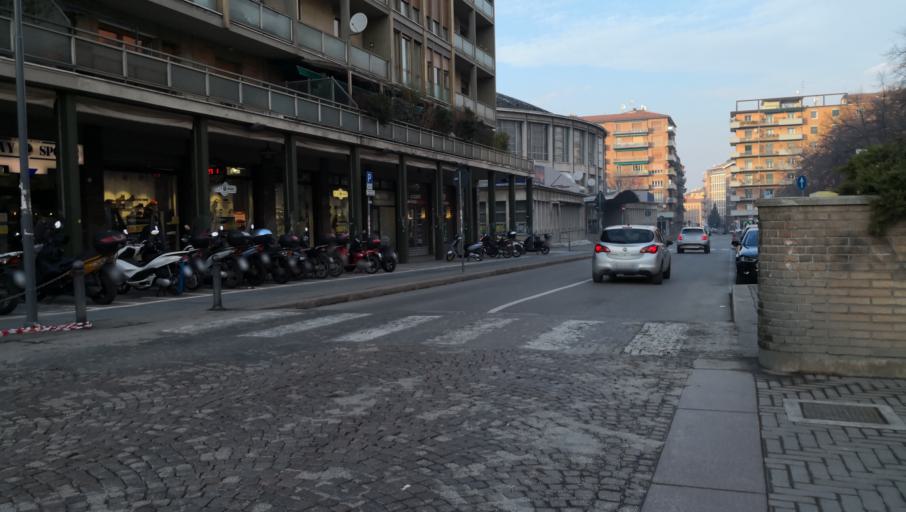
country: IT
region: Emilia-Romagna
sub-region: Provincia di Bologna
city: Bologna
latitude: 44.4989
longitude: 11.3328
